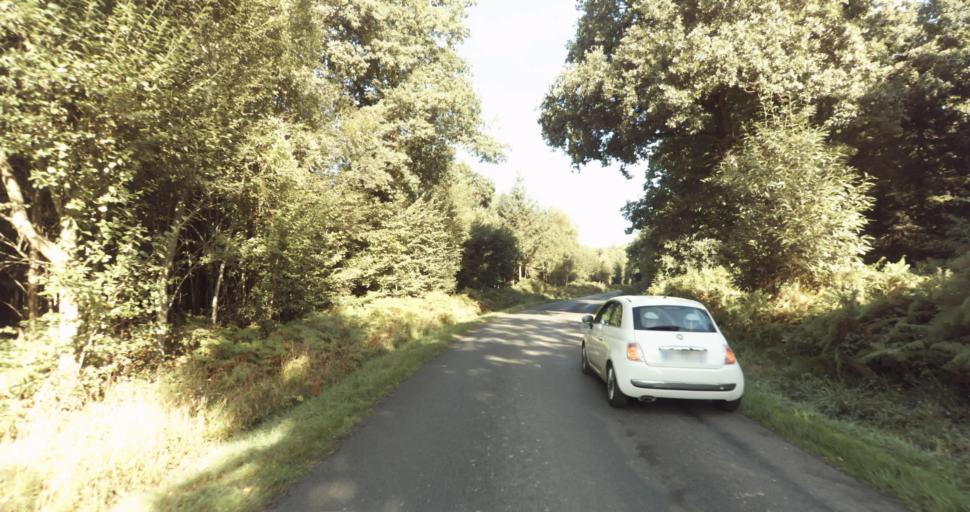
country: FR
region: Lower Normandy
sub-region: Departement de l'Orne
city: Vimoutiers
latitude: 48.9307
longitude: 0.2821
